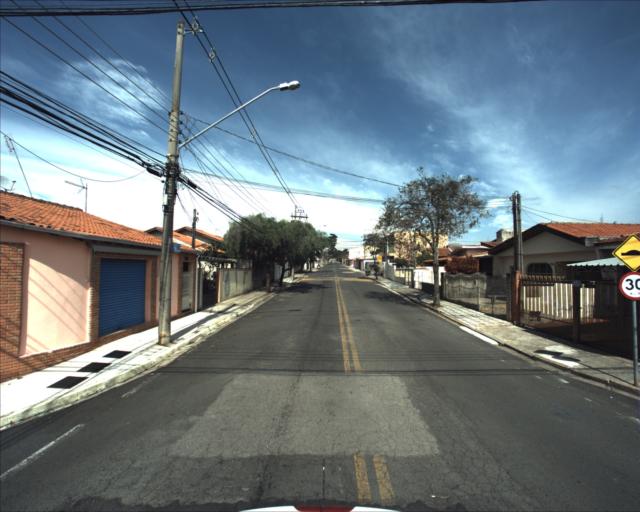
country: BR
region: Sao Paulo
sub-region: Sorocaba
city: Sorocaba
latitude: -23.5143
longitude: -47.5069
